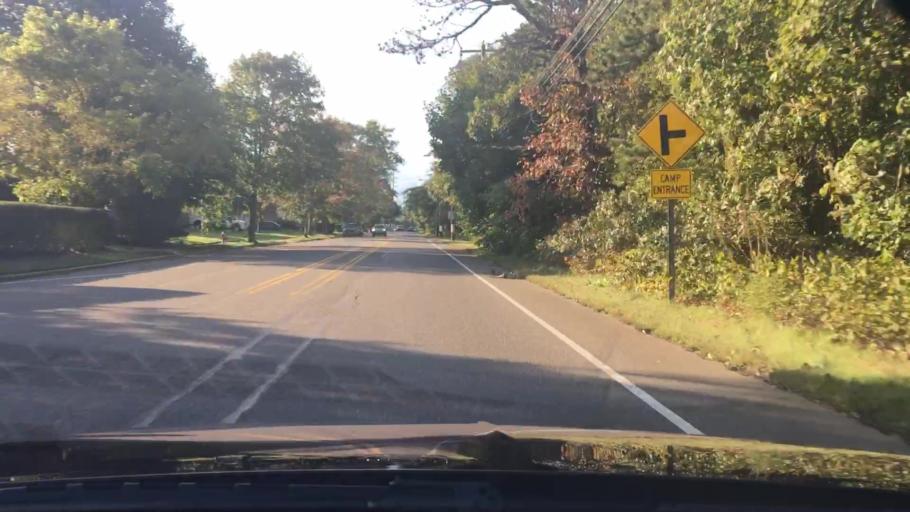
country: US
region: New York
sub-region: Suffolk County
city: Wheatley Heights
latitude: 40.7611
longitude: -73.3892
